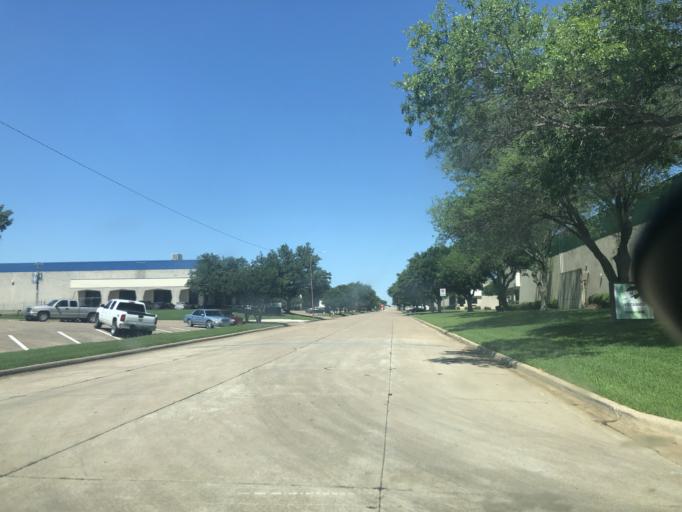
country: US
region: Texas
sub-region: Dallas County
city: Grand Prairie
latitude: 32.7829
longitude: -97.0426
